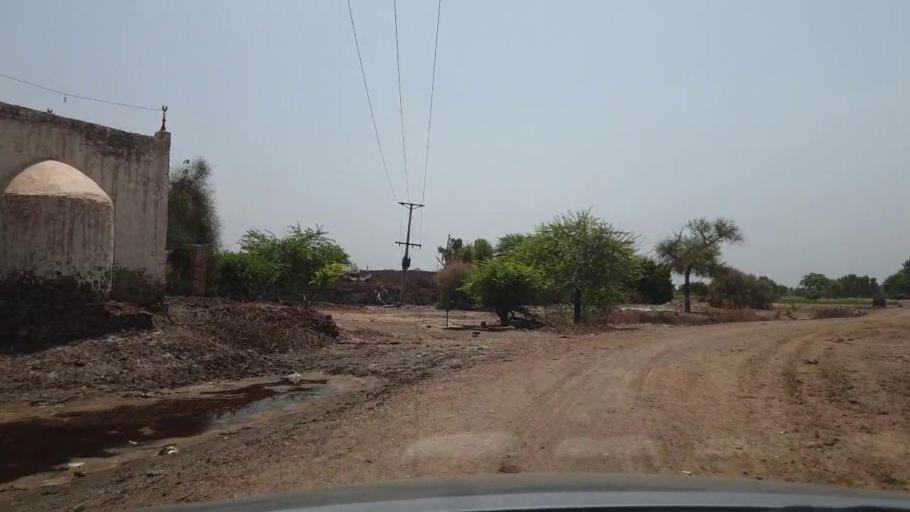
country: PK
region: Sindh
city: Madeji
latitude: 27.7737
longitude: 68.4056
